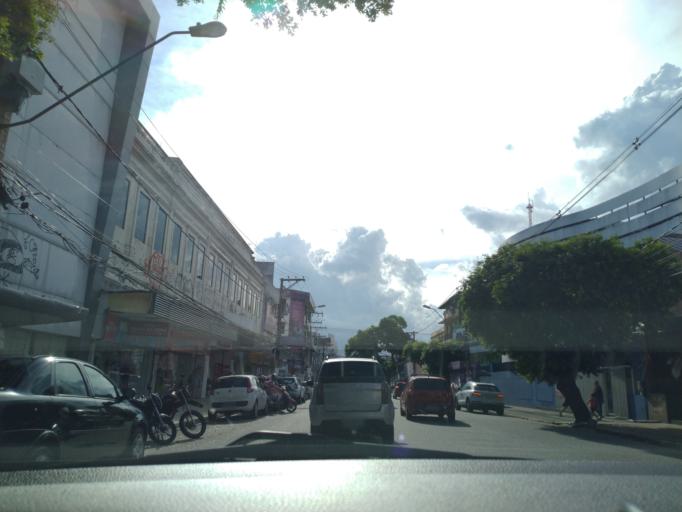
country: BR
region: Para
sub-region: Belem
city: Belem
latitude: -1.4589
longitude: -48.4928
